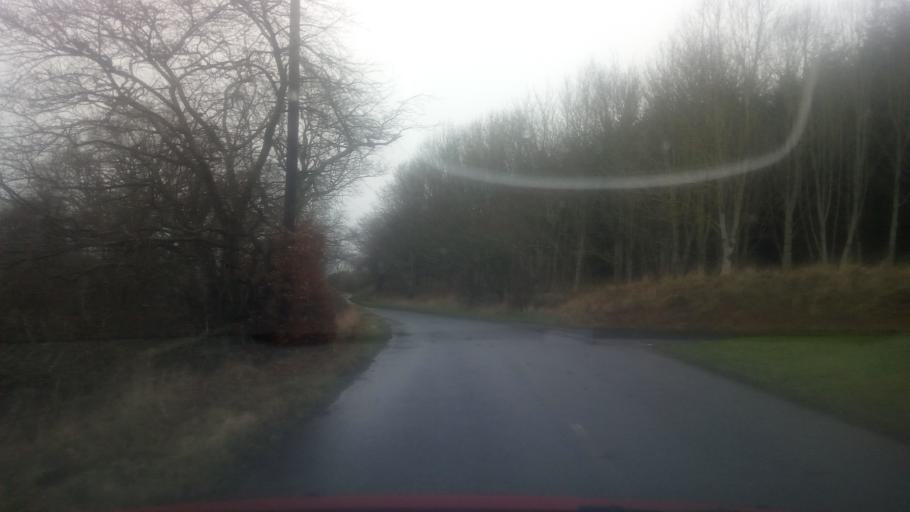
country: GB
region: Scotland
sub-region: The Scottish Borders
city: Earlston
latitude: 55.6206
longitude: -2.6653
